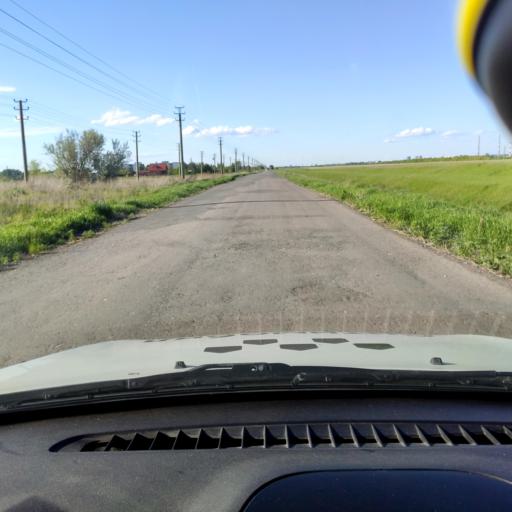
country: RU
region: Samara
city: Podstepki
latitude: 53.5272
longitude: 49.1968
